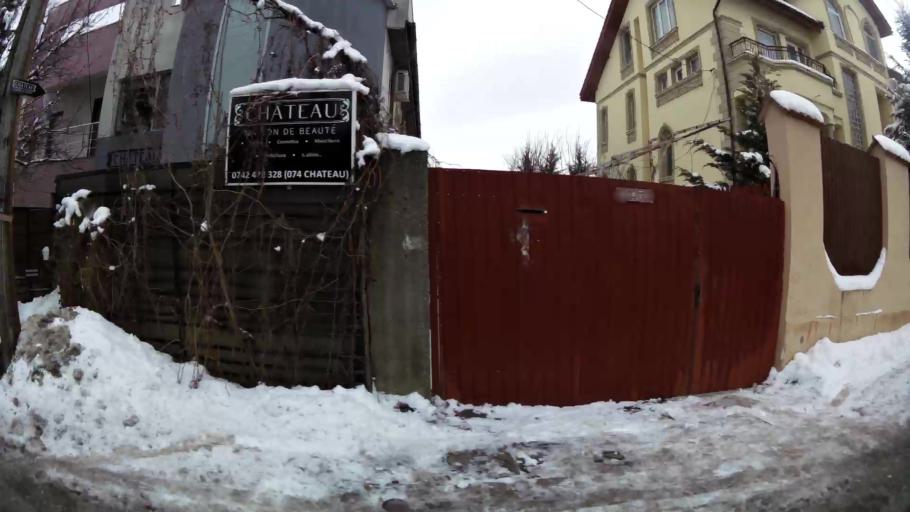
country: RO
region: Ilfov
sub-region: Comuna Otopeni
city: Otopeni
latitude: 44.5133
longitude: 26.1055
